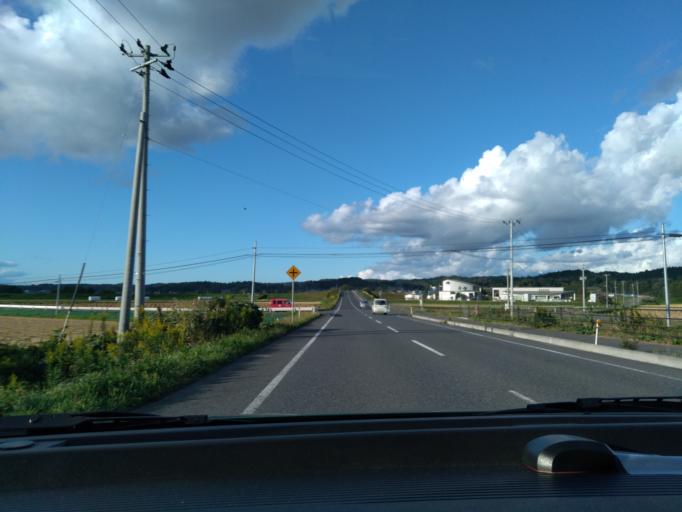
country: JP
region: Iwate
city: Ichinoseki
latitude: 38.8171
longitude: 141.1987
